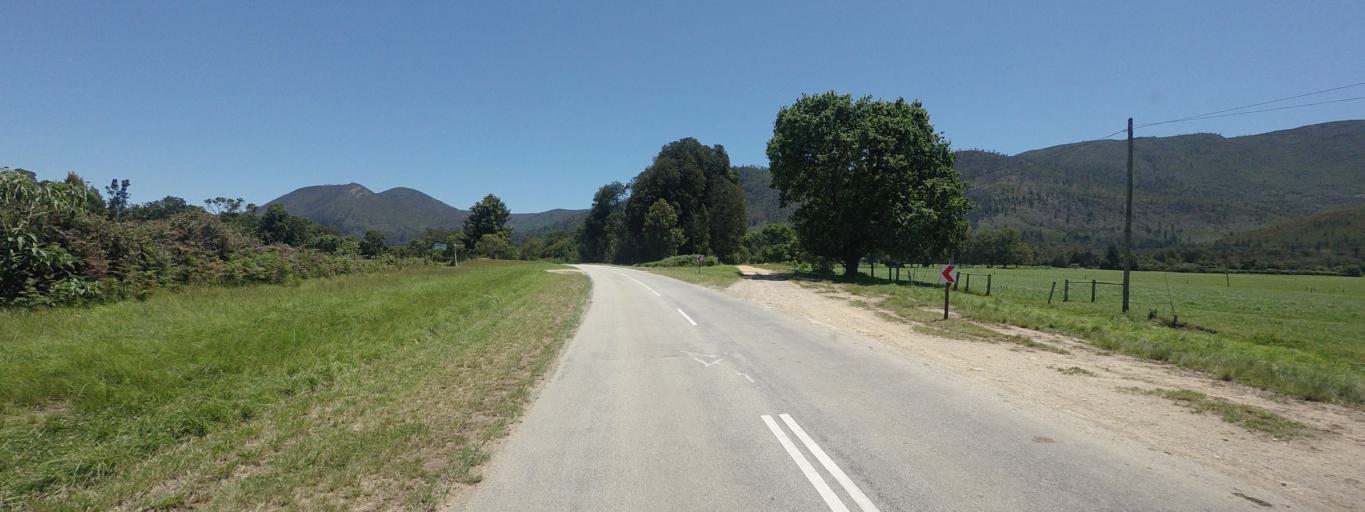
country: ZA
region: Western Cape
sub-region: Eden District Municipality
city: Plettenberg Bay
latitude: -33.9390
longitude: 23.5096
